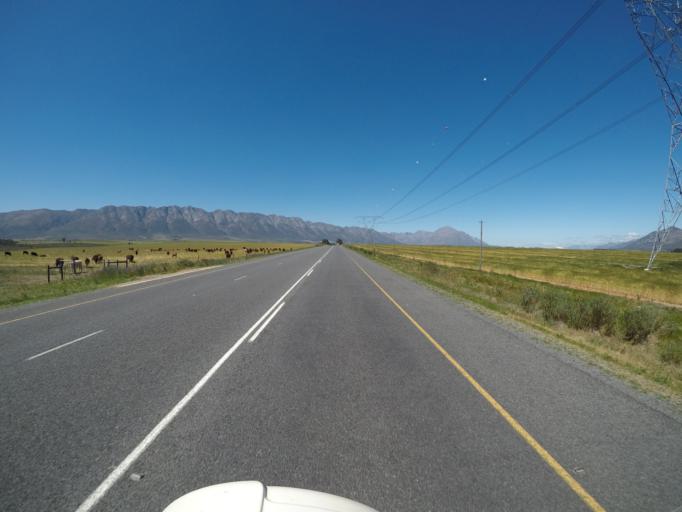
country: ZA
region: Western Cape
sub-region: Cape Winelands District Municipality
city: Ceres
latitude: -33.3153
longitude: 19.1281
